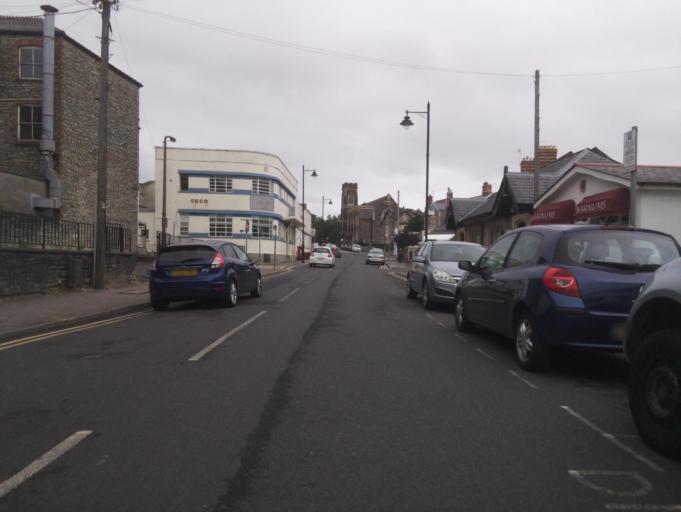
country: GB
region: Wales
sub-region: Vale of Glamorgan
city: Penarth
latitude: 51.4390
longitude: -3.1735
